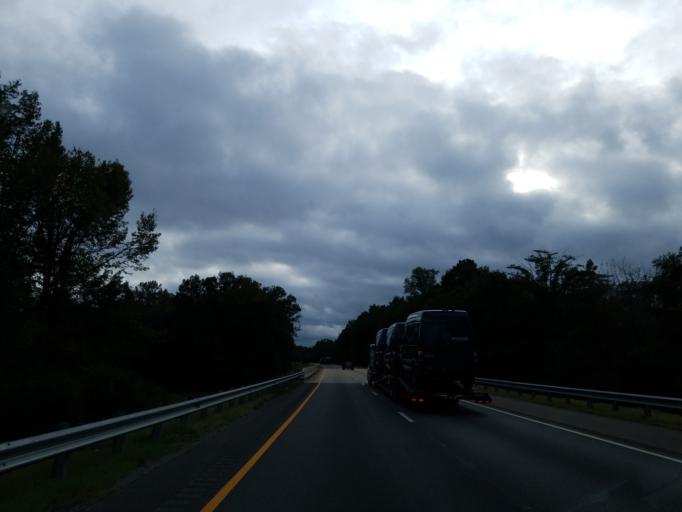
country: US
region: Alabama
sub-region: Tuscaloosa County
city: Tuscaloosa
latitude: 33.1323
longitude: -87.6404
